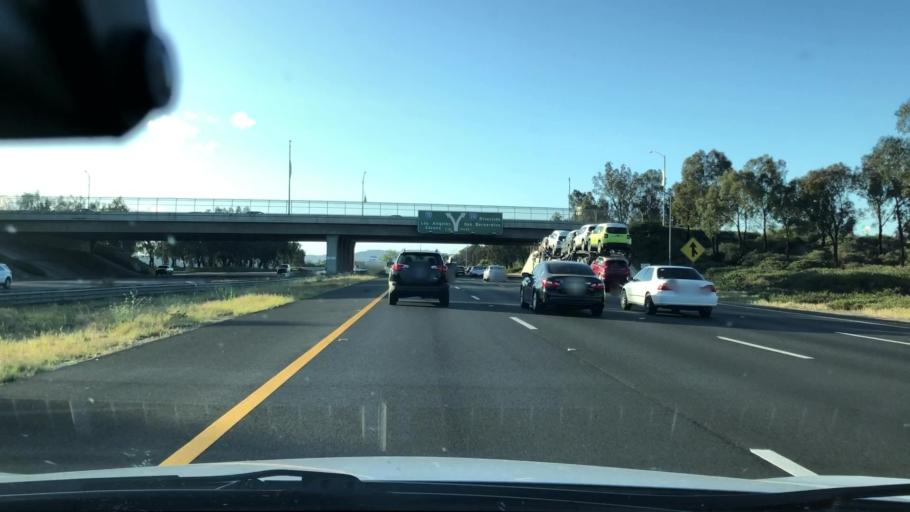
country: US
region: California
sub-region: Riverside County
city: Temecula
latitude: 33.5215
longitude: -117.1622
